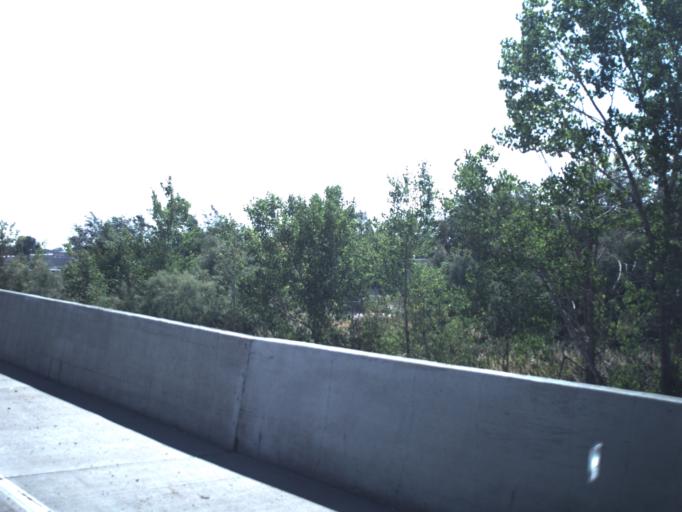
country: US
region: Utah
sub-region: Salt Lake County
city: Murray
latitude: 40.6735
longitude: -111.9022
